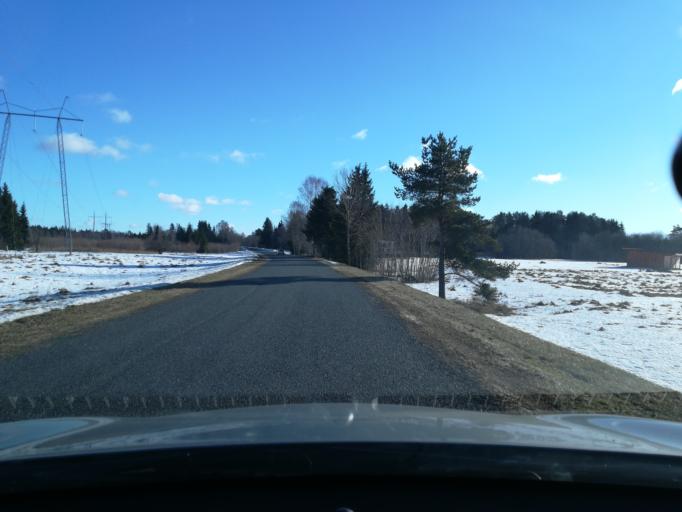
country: EE
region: Raplamaa
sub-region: Kohila vald
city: Kohila
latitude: 59.2348
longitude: 24.7601
